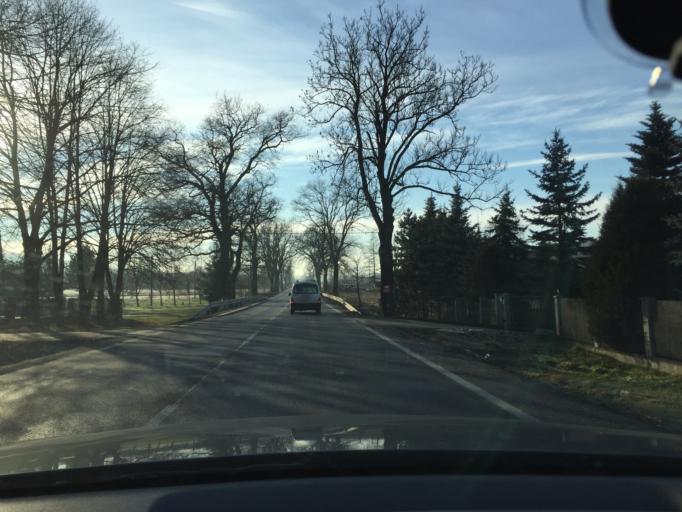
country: PL
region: Lesser Poland Voivodeship
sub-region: Powiat myslenicki
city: Krzywaczka
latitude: 49.8885
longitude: 19.8208
